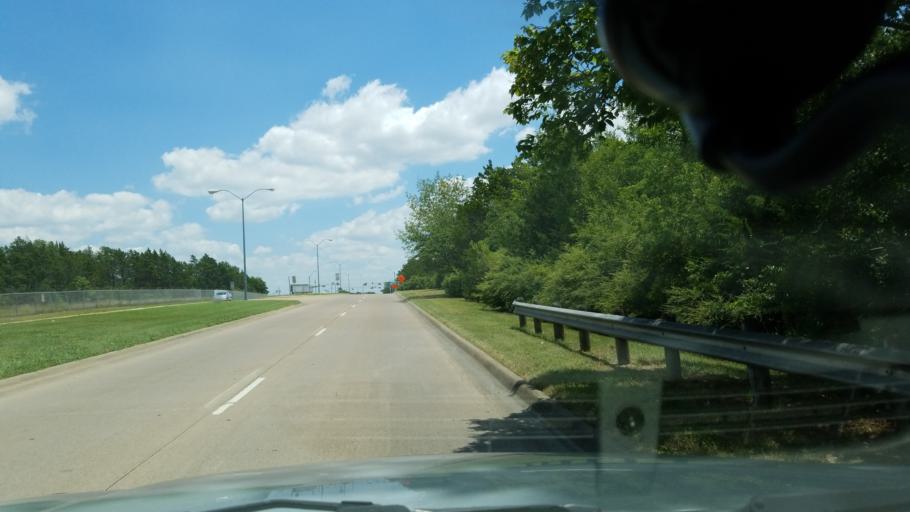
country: US
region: Texas
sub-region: Dallas County
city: Duncanville
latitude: 32.6710
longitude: -96.8652
